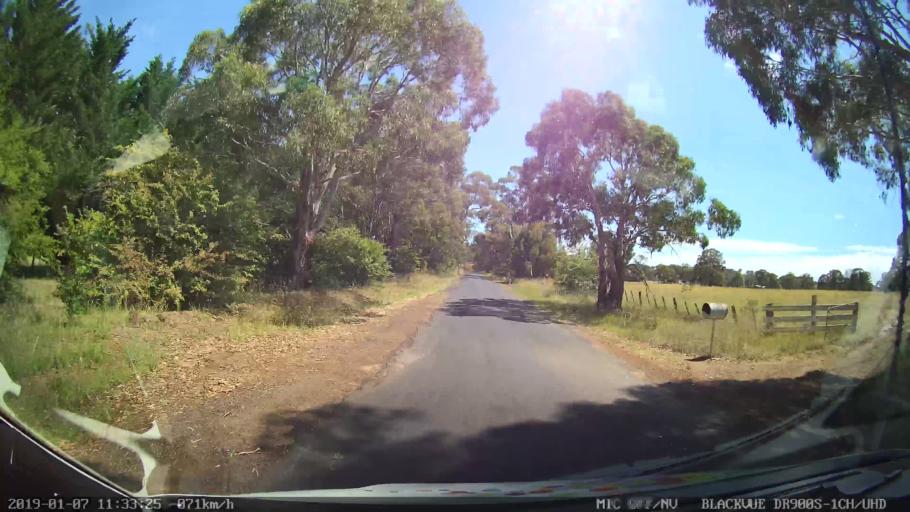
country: AU
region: New South Wales
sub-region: Armidale Dumaresq
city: Armidale
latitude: -30.4002
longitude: 151.5610
